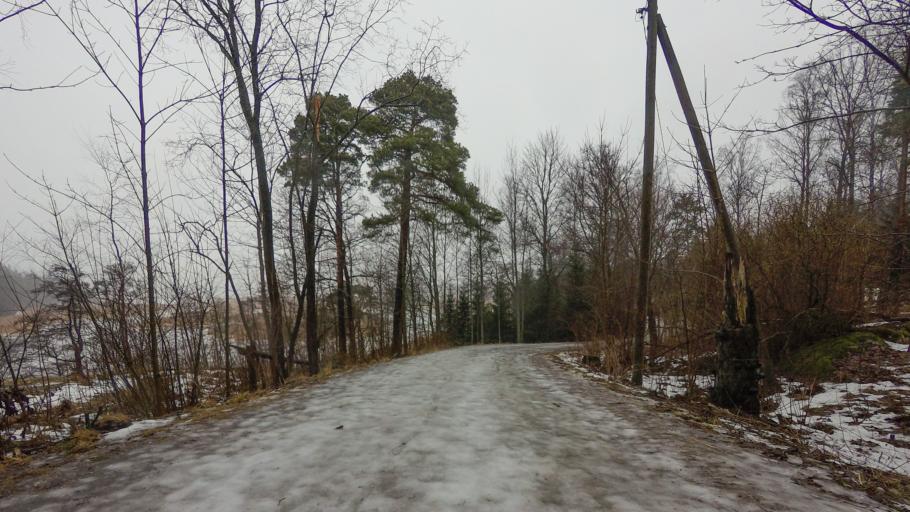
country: FI
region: Uusimaa
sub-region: Helsinki
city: Helsinki
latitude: 60.1964
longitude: 25.0250
